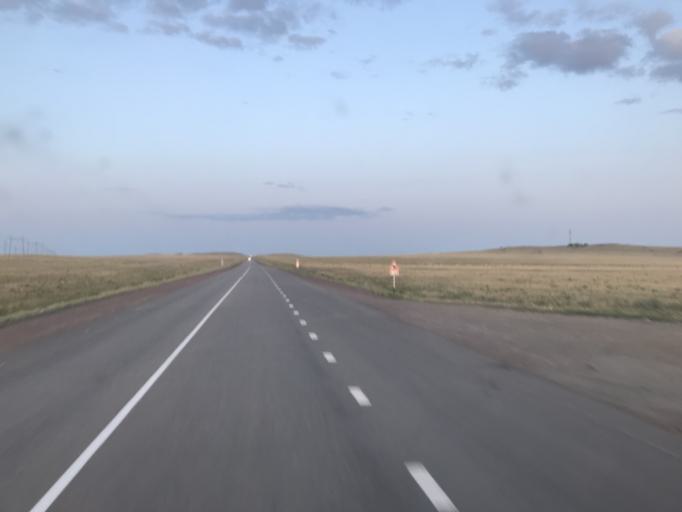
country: KZ
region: Aqmola
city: Astrakhan
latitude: 51.8060
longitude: 69.1822
